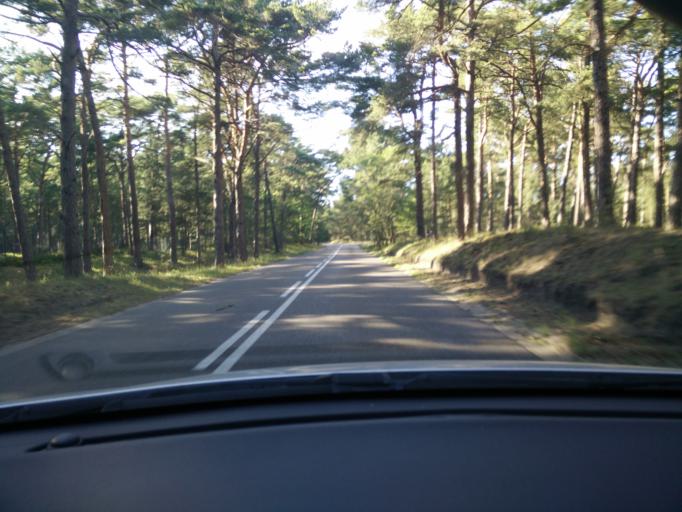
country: PL
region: Pomeranian Voivodeship
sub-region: Powiat pucki
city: Jastarnia
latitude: 54.6638
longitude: 18.7461
